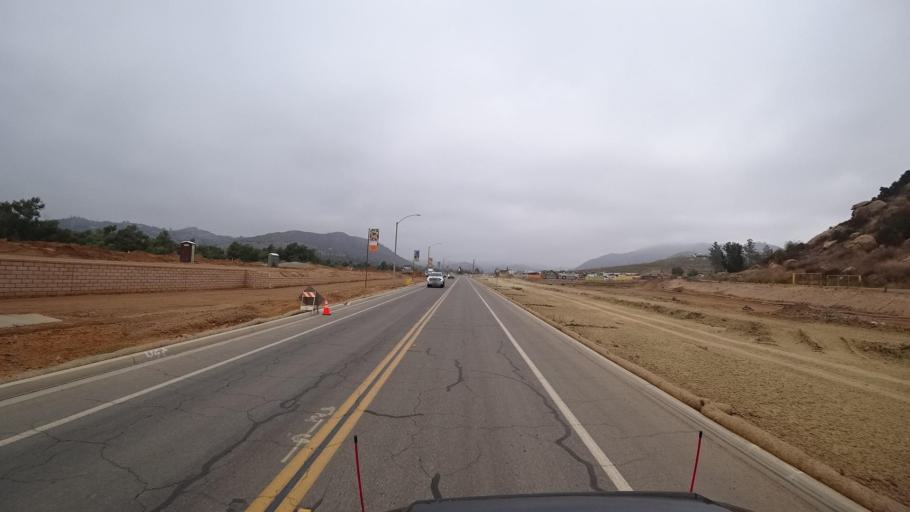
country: US
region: California
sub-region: San Diego County
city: Rainbow
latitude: 33.3413
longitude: -117.1489
